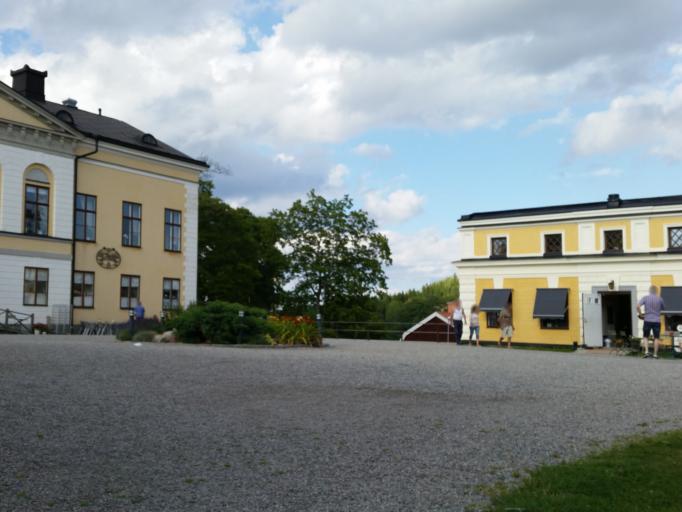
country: SE
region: Soedermanland
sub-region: Strangnas Kommun
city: Mariefred
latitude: 59.2461
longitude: 17.3098
